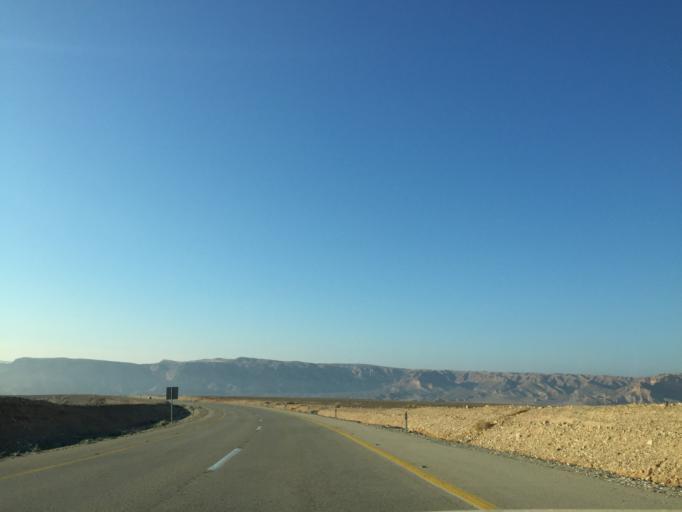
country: IL
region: Southern District
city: Mitzpe Ramon
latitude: 30.3431
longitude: 34.9507
